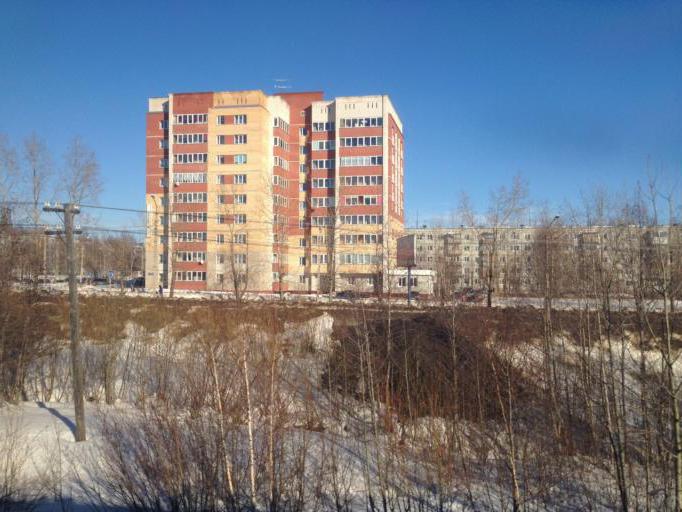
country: RU
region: Komi Republic
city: Ezhva
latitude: 61.7941
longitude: 50.7385
